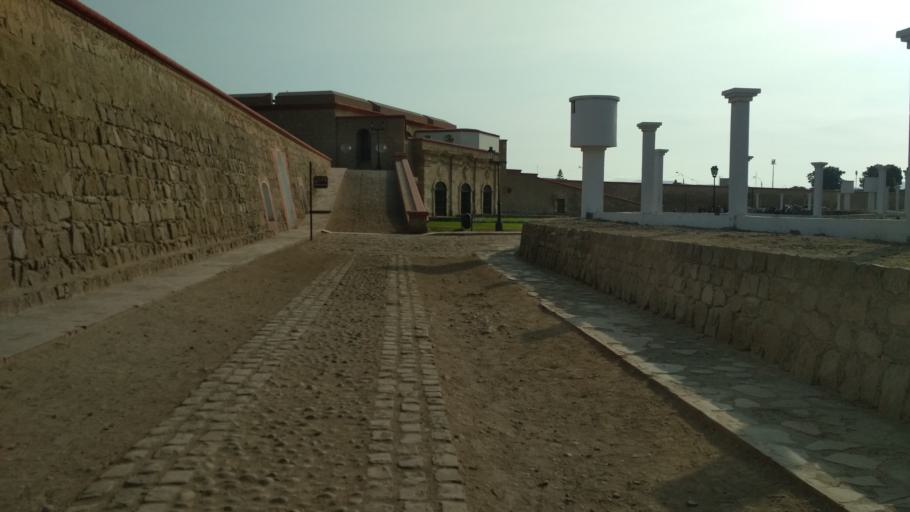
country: PE
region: Callao
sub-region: Callao
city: Callao
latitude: -12.0630
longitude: -77.1482
